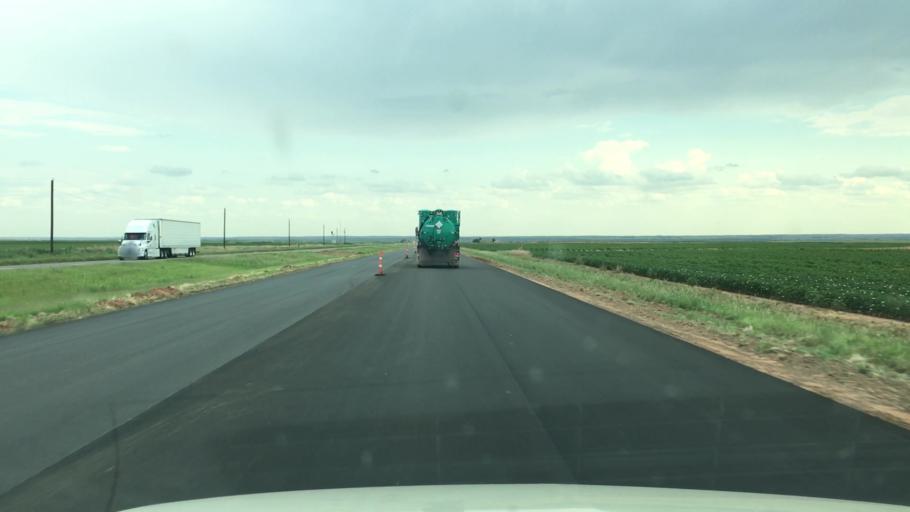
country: US
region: Texas
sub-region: Hall County
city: Memphis
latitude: 34.6296
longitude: -100.4756
